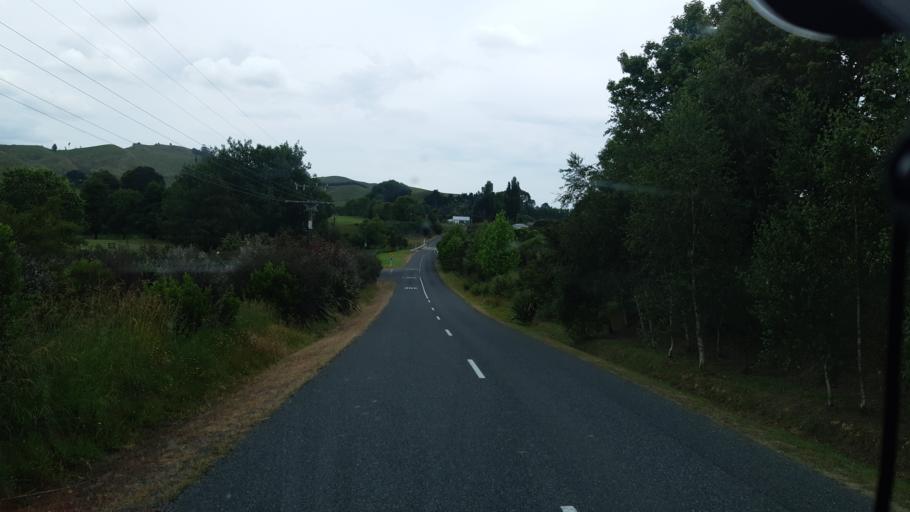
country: NZ
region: Waikato
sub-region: Waikato District
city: Raglan
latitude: -37.8483
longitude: 175.0360
